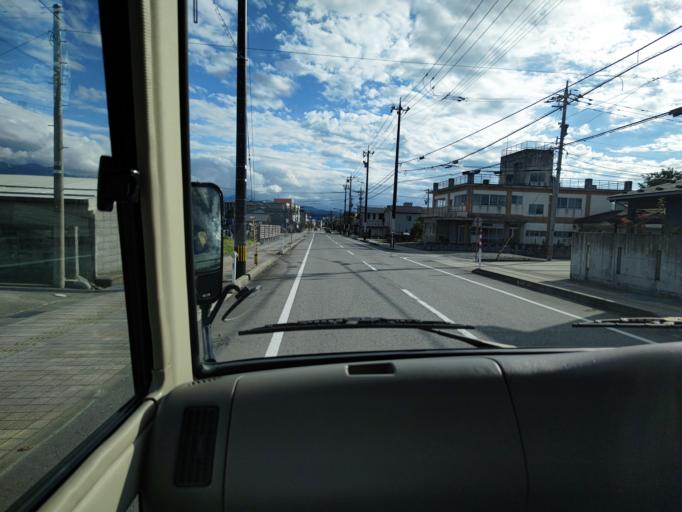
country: JP
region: Toyama
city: Nyuzen
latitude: 36.8751
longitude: 137.4469
